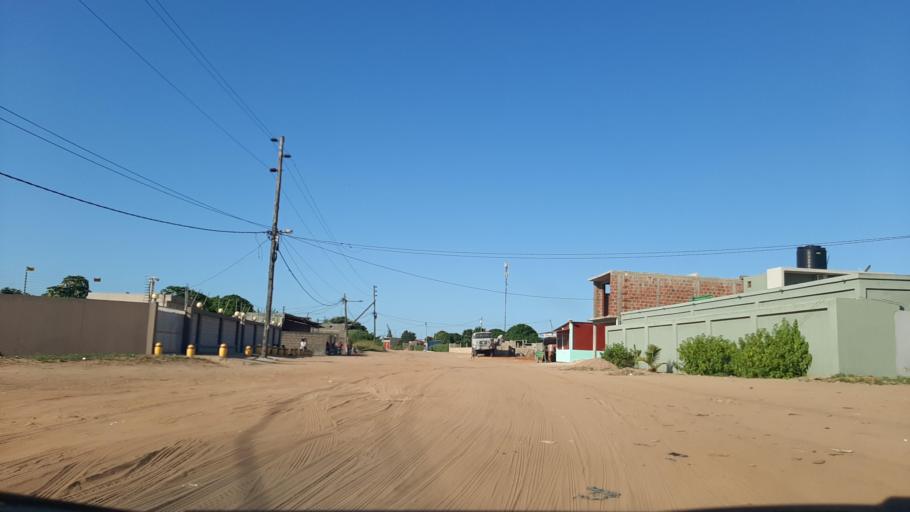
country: MZ
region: Maputo City
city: Maputo
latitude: -25.8001
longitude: 32.5504
